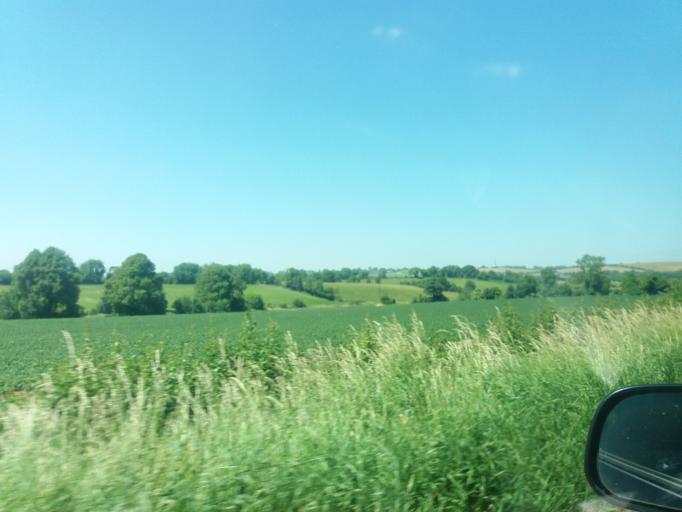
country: IE
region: Leinster
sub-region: An Mhi
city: Stamullin
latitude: 53.5774
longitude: -6.3120
